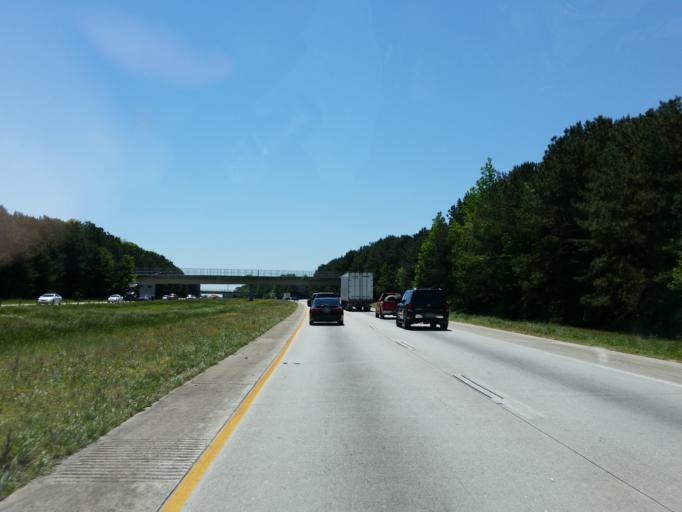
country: US
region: Georgia
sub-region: Clayton County
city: Lake City
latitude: 33.5850
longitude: -84.2810
